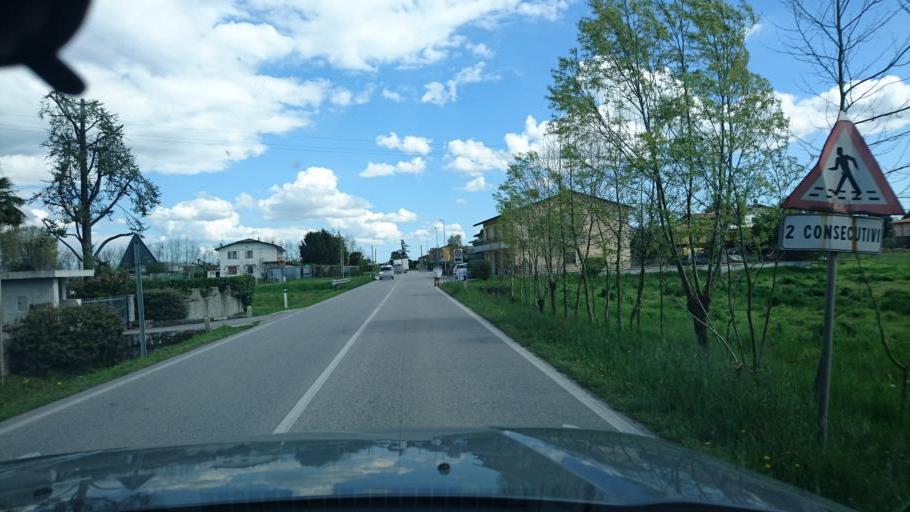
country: IT
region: Veneto
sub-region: Provincia di Padova
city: Santa Maria di Non
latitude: 45.5152
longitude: 11.8506
